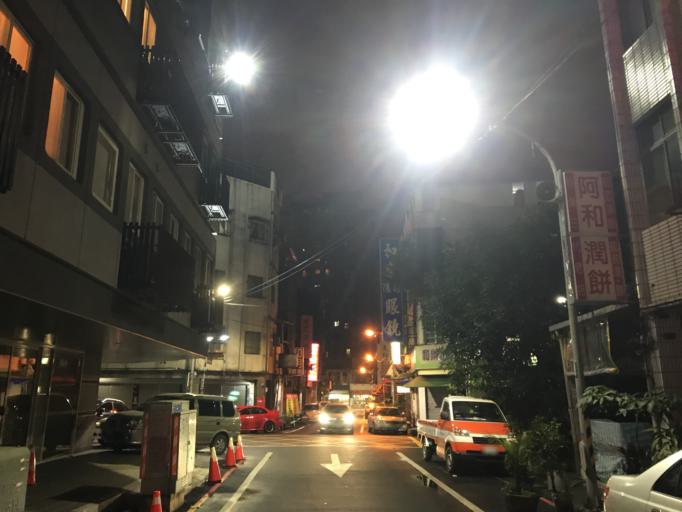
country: TW
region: Taiwan
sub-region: Taoyuan
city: Taoyuan
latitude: 24.9955
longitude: 121.3114
